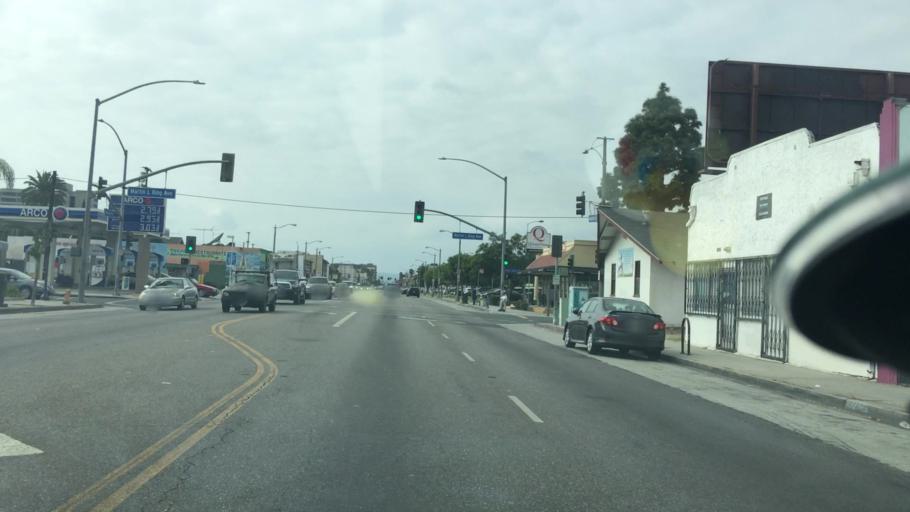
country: US
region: California
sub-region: Los Angeles County
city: Long Beach
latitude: 33.7826
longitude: -118.1802
